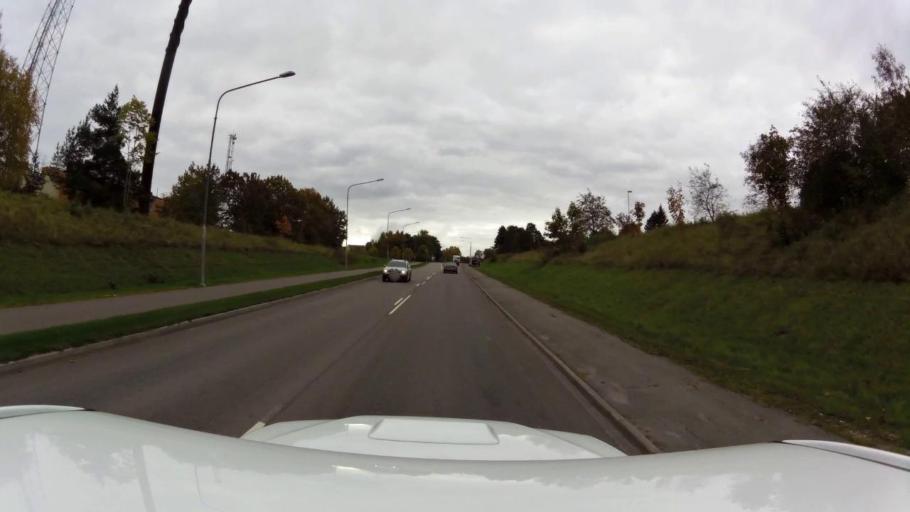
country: SE
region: OEstergoetland
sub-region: Linkopings Kommun
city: Ljungsbro
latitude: 58.5001
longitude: 15.5052
